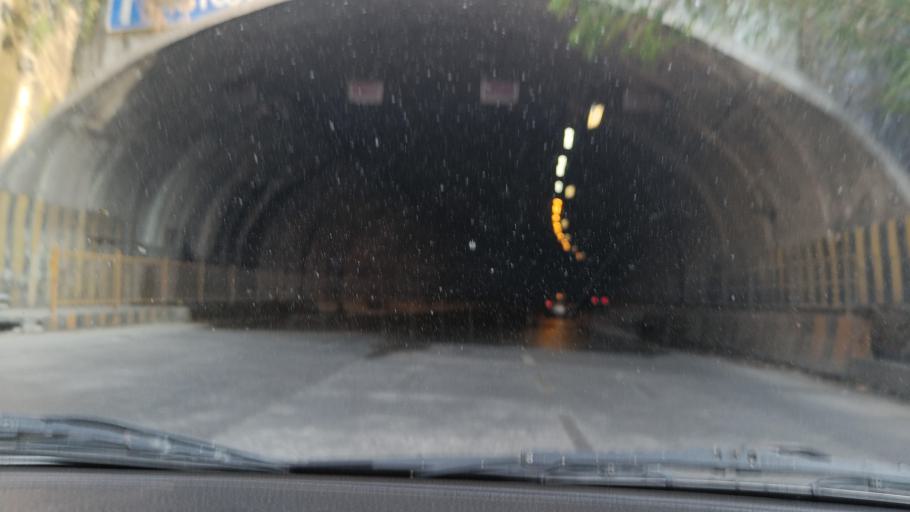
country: IN
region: Maharashtra
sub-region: Mumbai Suburban
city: Mumbai
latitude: 19.0393
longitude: 72.9090
